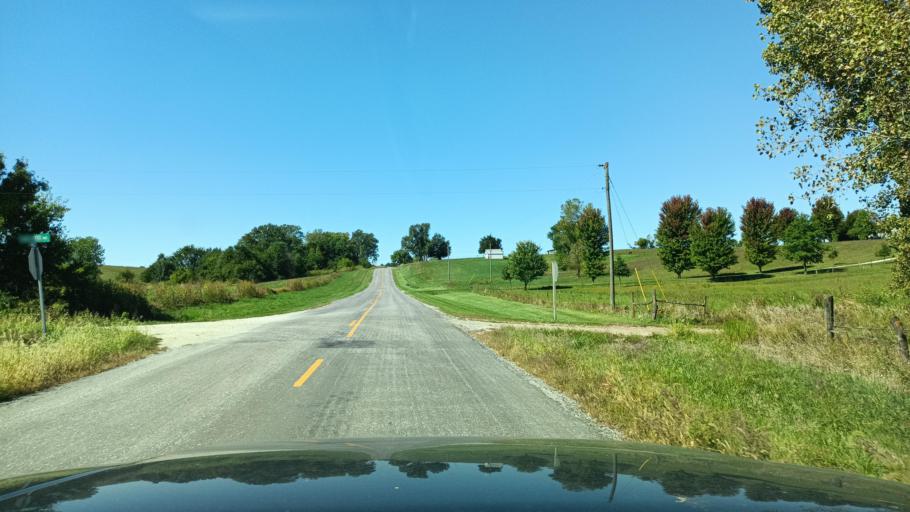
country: US
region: Missouri
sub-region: Adair County
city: Kirksville
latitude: 40.3299
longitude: -92.5535
